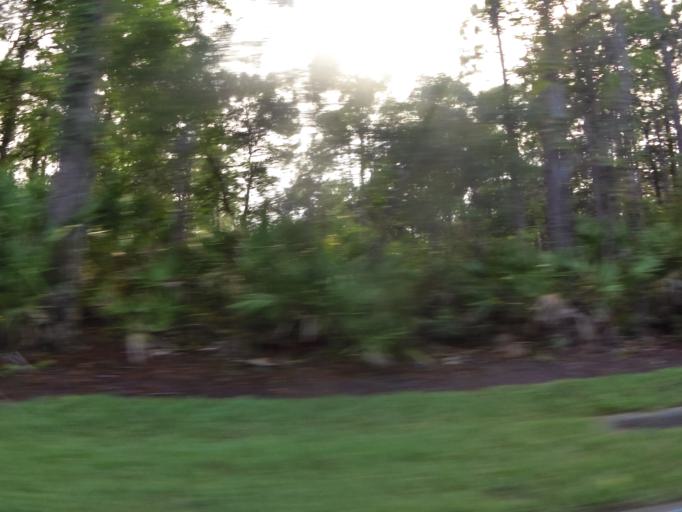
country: US
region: Florida
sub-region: Saint Johns County
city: Fruit Cove
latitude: 30.2130
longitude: -81.5394
